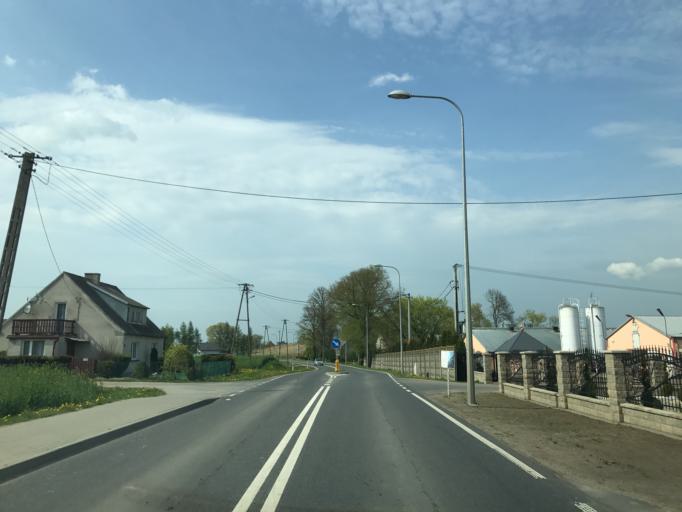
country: PL
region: Warmian-Masurian Voivodeship
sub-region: Powiat dzialdowski
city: Rybno
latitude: 53.3872
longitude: 19.8140
